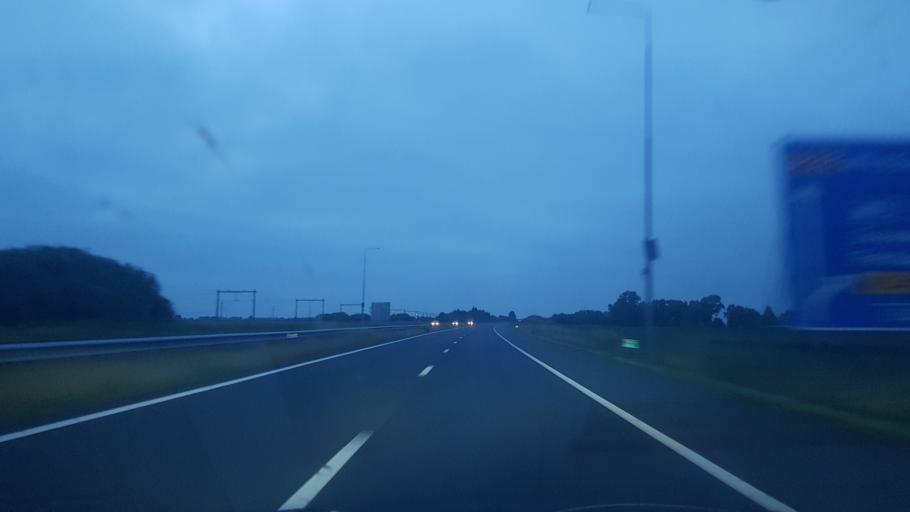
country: NL
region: Friesland
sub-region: Gemeente Boarnsterhim
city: Grou
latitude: 53.1002
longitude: 5.8183
